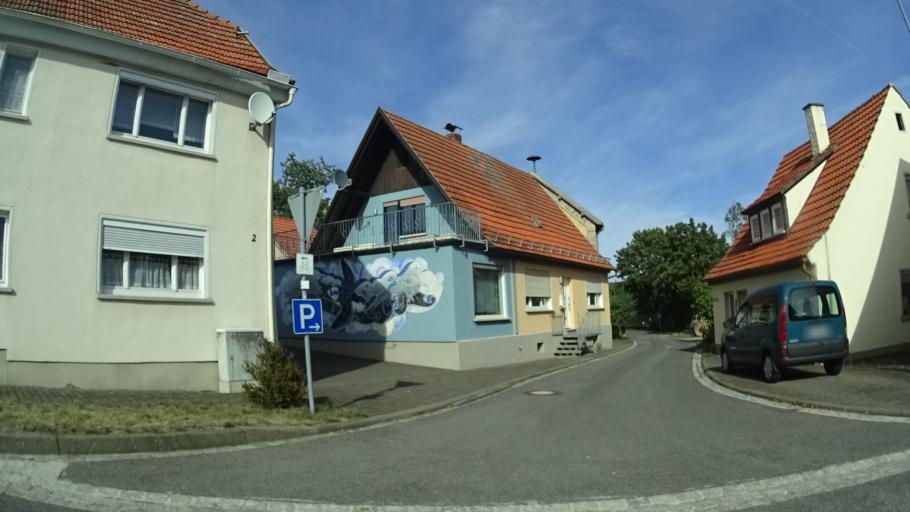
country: DE
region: Thuringia
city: Melpers
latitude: 50.5486
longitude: 10.1964
